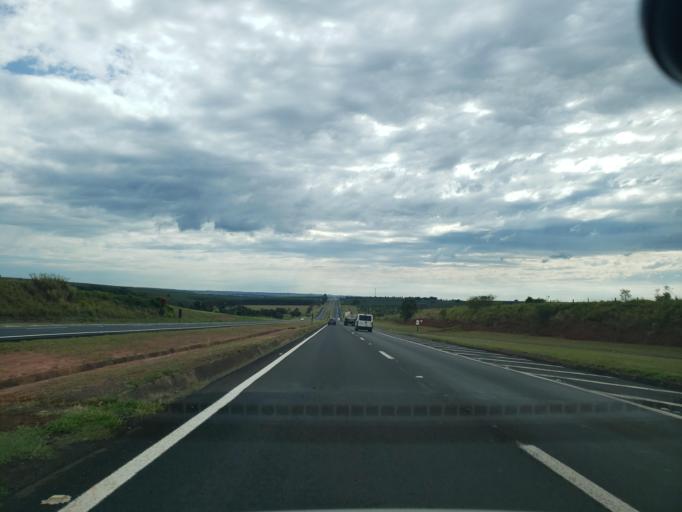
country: BR
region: Sao Paulo
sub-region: Bauru
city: Bauru
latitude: -22.1827
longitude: -49.2181
